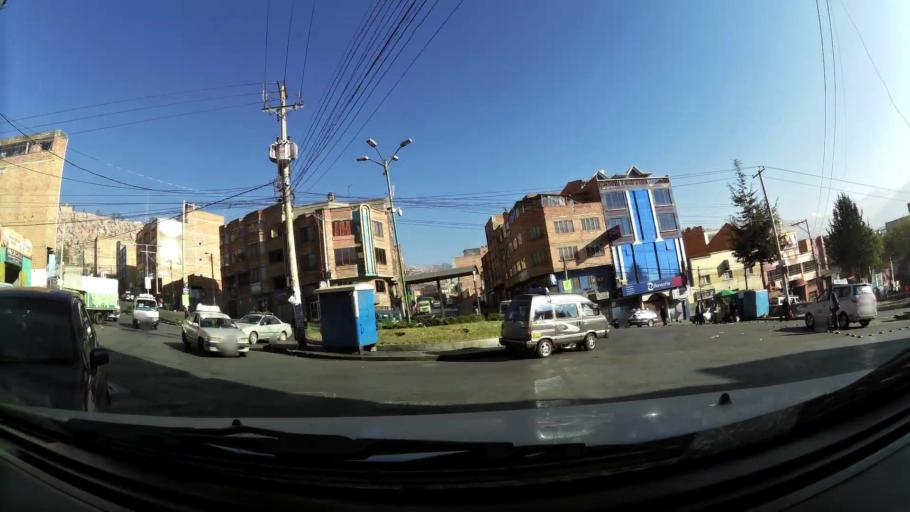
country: BO
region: La Paz
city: La Paz
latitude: -16.5005
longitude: -68.1528
